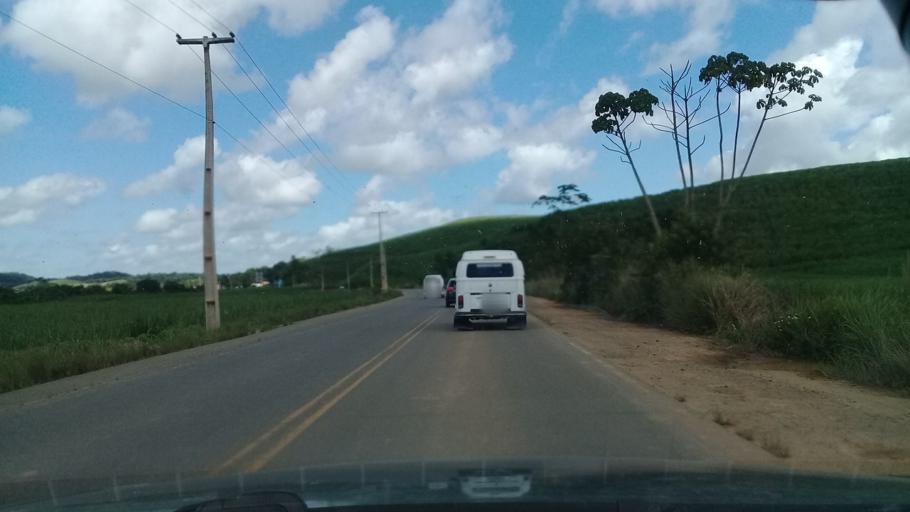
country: BR
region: Pernambuco
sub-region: Sirinhaem
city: Sirinhaem
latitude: -8.4988
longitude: -35.0945
